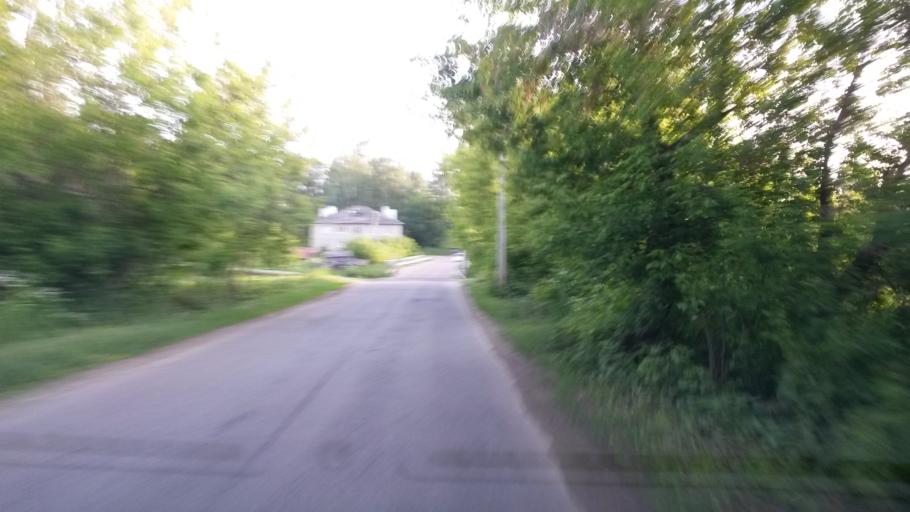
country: RU
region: Jaroslavl
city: Yaroslavl
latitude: 57.7017
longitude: 39.8262
